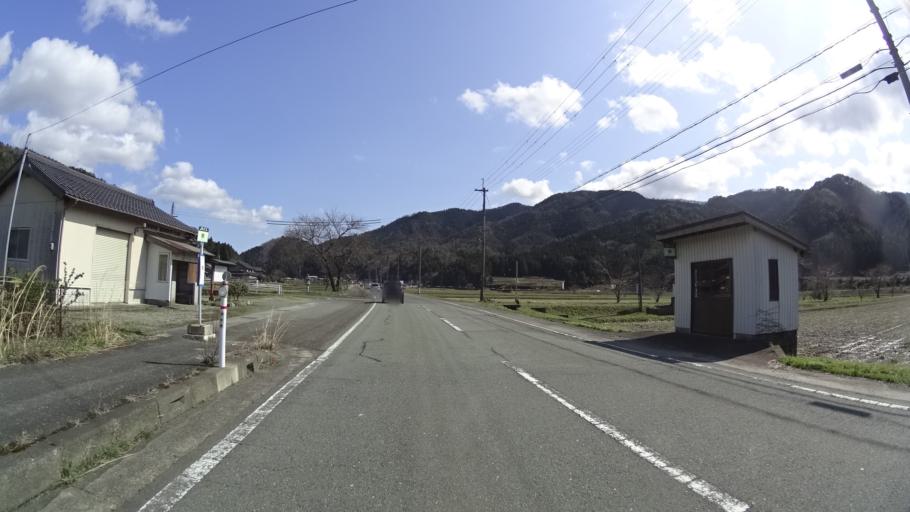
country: JP
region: Fukui
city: Obama
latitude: 35.4539
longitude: 135.8814
